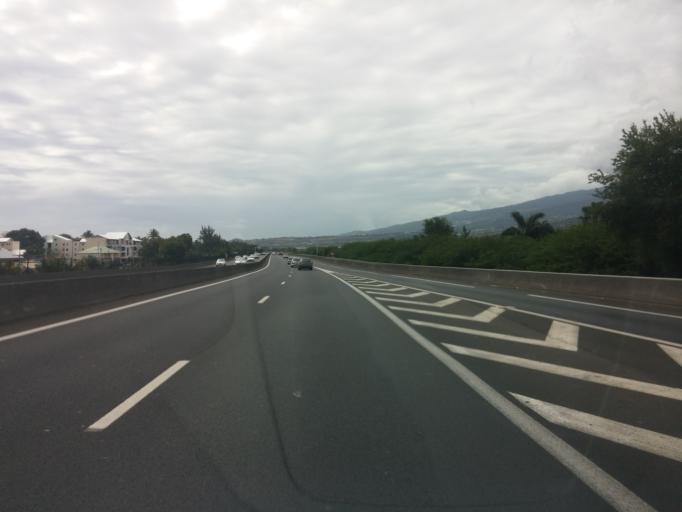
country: RE
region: Reunion
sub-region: Reunion
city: Saint-Paul
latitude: -21.0085
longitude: 55.2780
